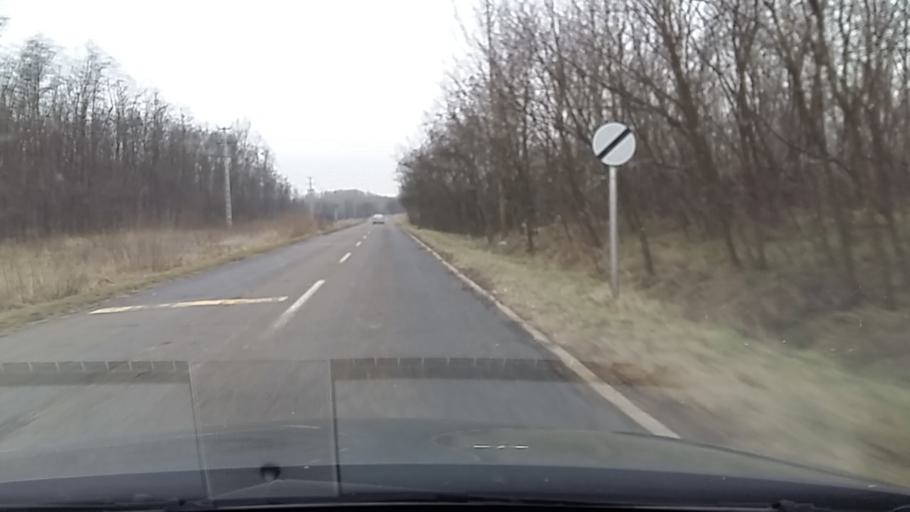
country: HU
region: Szabolcs-Szatmar-Bereg
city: Nyirbogdany
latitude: 48.0842
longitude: 21.8633
